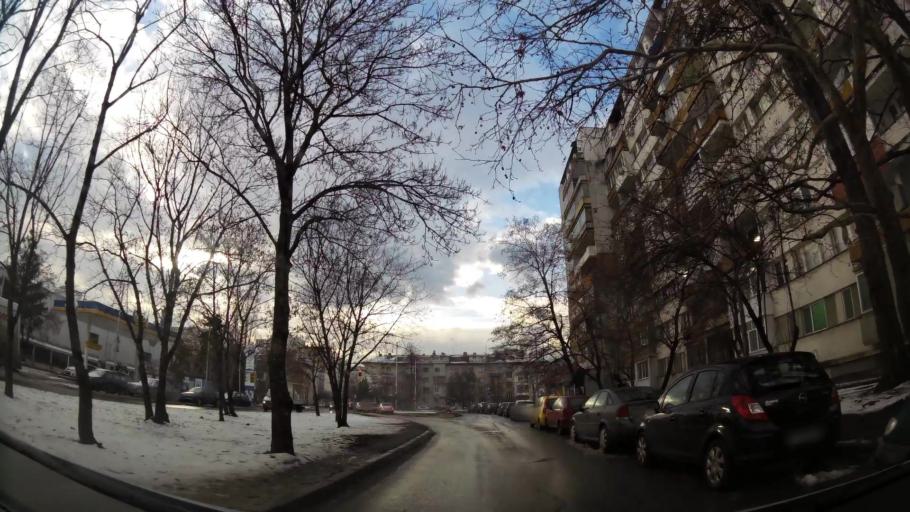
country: BG
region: Sofia-Capital
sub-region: Stolichna Obshtina
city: Sofia
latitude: 42.7028
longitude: 23.2833
